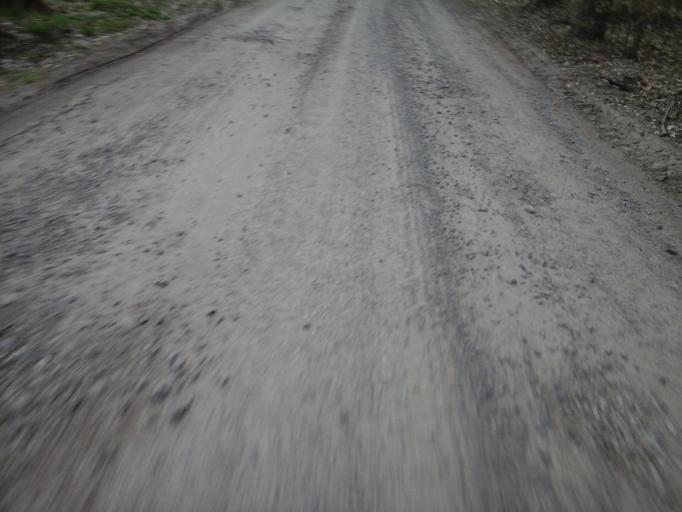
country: PL
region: West Pomeranian Voivodeship
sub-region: Powiat choszczenski
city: Bierzwnik
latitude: 53.0177
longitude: 15.6491
